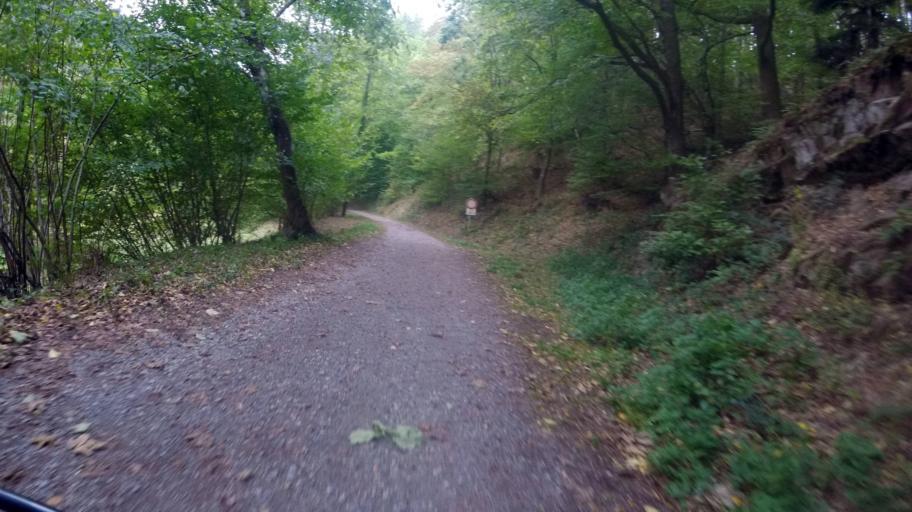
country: DE
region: Baden-Wuerttemberg
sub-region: Karlsruhe Region
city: Loffenau
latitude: 48.7669
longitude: 8.3773
